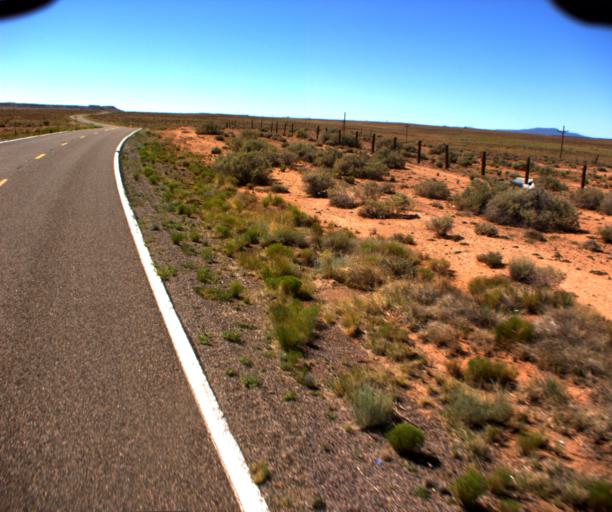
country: US
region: Arizona
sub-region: Coconino County
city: LeChee
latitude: 35.1144
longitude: -110.8711
